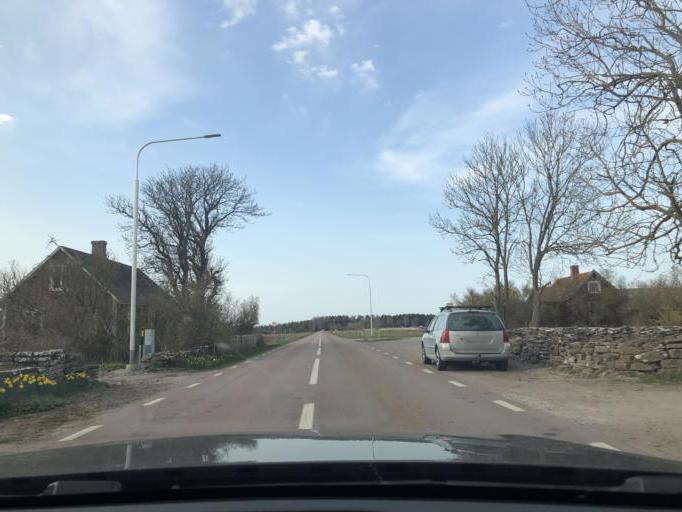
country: SE
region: Kalmar
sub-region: Morbylanga Kommun
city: Sodra Sandby
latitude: 56.5673
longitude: 16.6186
